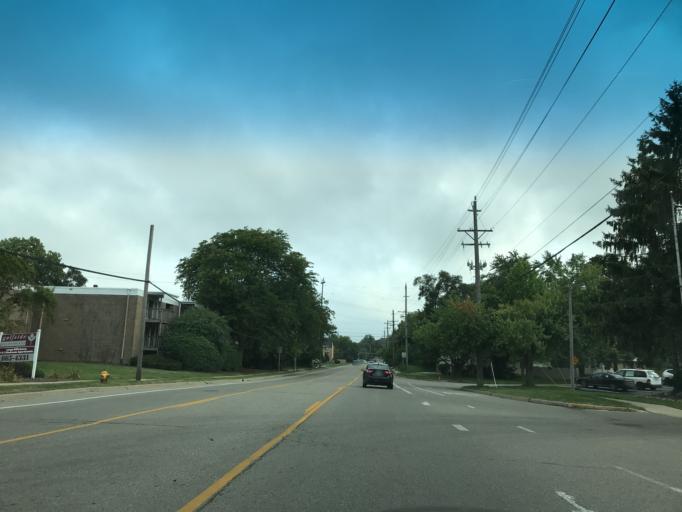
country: US
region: Michigan
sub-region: Washtenaw County
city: Ypsilanti
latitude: 42.2489
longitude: -83.6611
